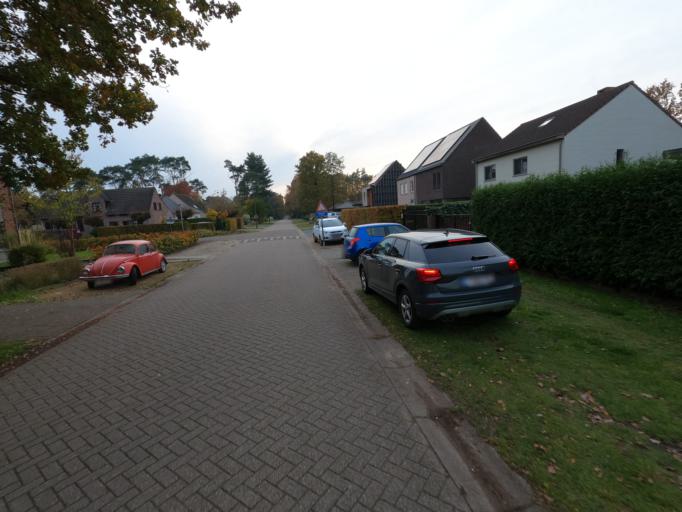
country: BE
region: Flanders
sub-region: Provincie Antwerpen
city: Wuustwezel
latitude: 51.3491
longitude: 4.5496
